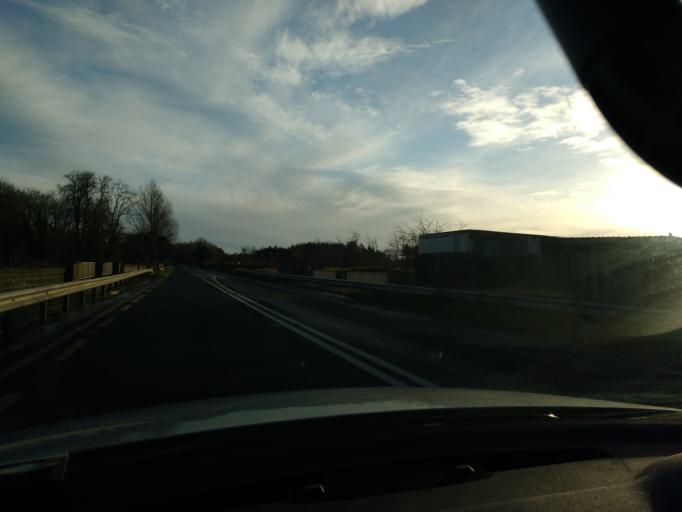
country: IE
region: Munster
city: Thurles
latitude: 52.6641
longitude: -7.8050
